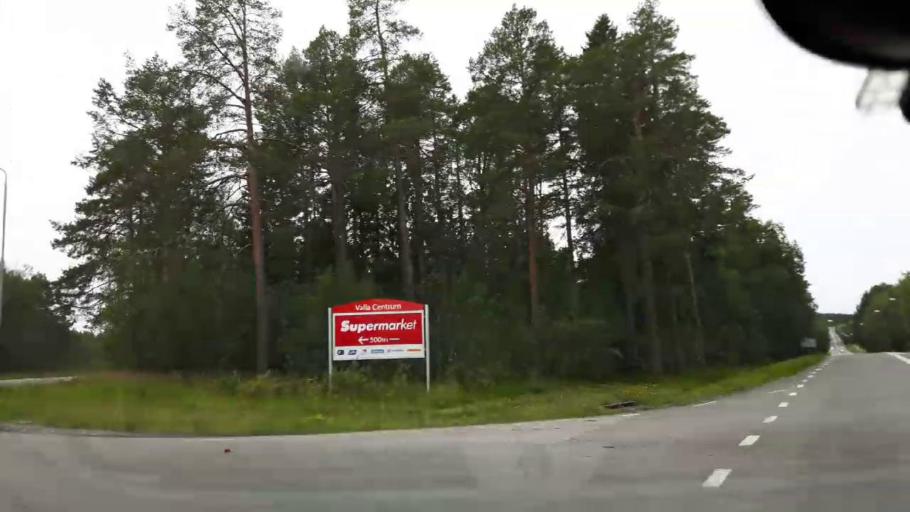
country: SE
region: Jaemtland
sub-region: OEstersunds Kommun
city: Ostersund
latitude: 63.1719
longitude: 14.5729
